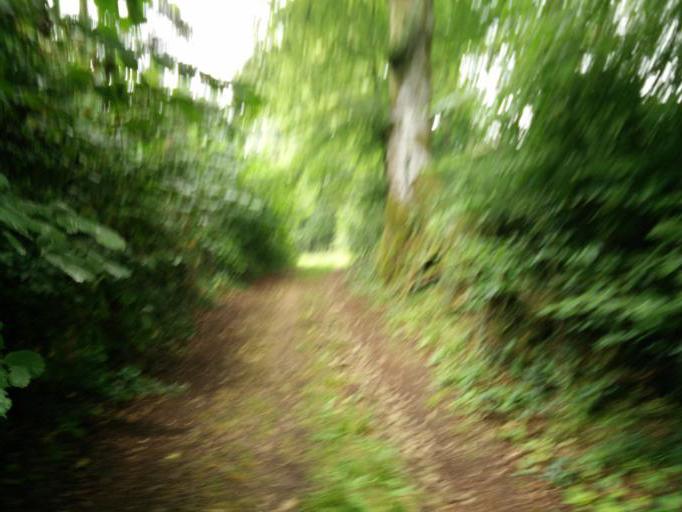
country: LU
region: Luxembourg
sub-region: Canton de Luxembourg
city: Bertrange
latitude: 49.6371
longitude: 6.0476
